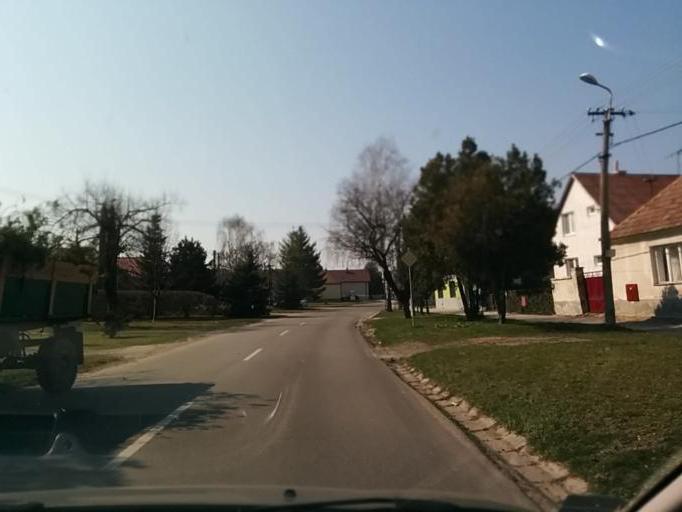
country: SK
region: Trnavsky
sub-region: Okres Galanta
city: Galanta
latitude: 48.2823
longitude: 17.7566
